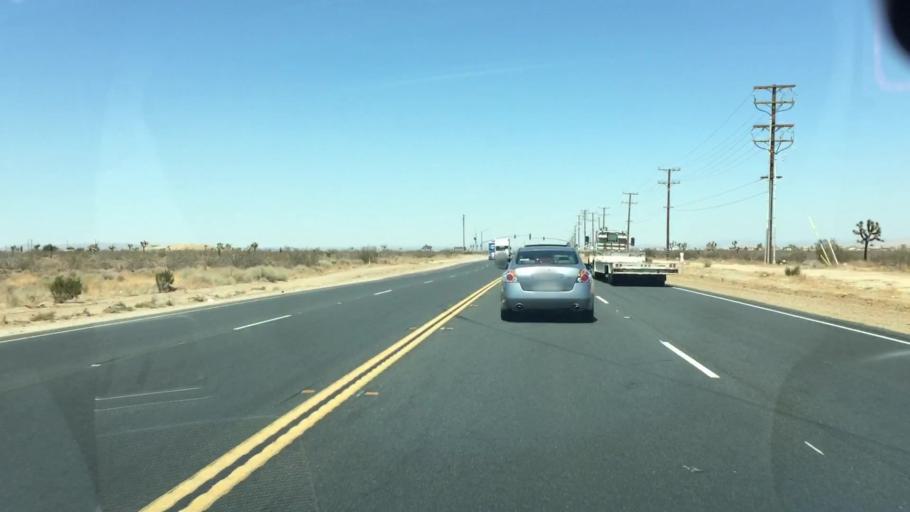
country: US
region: California
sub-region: San Bernardino County
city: Mountain View Acres
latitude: 34.4526
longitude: -117.3996
